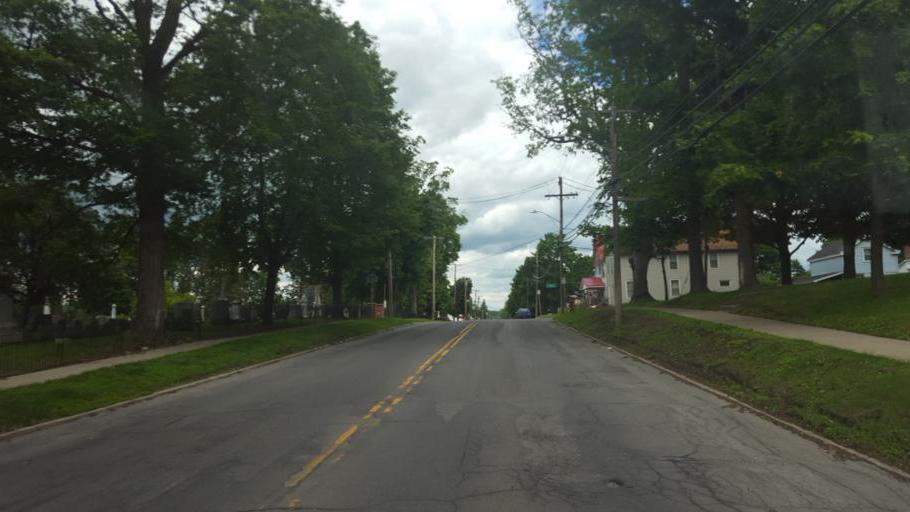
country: US
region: New York
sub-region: Herkimer County
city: Mohawk
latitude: 43.0054
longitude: -75.0064
